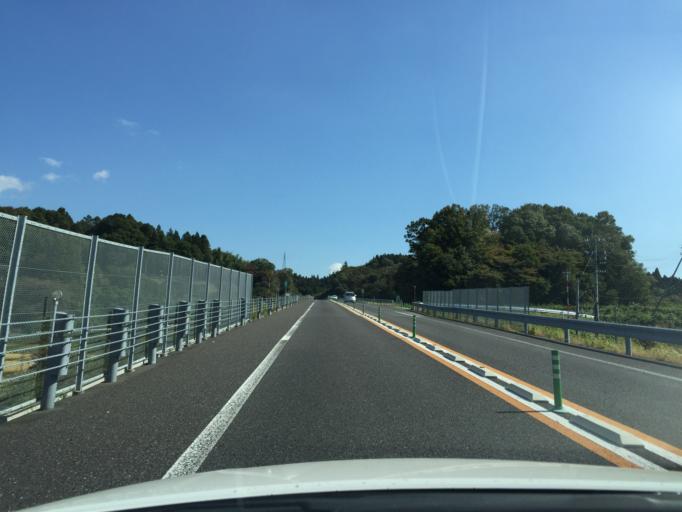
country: JP
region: Fukushima
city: Ishikawa
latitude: 37.2008
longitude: 140.4575
